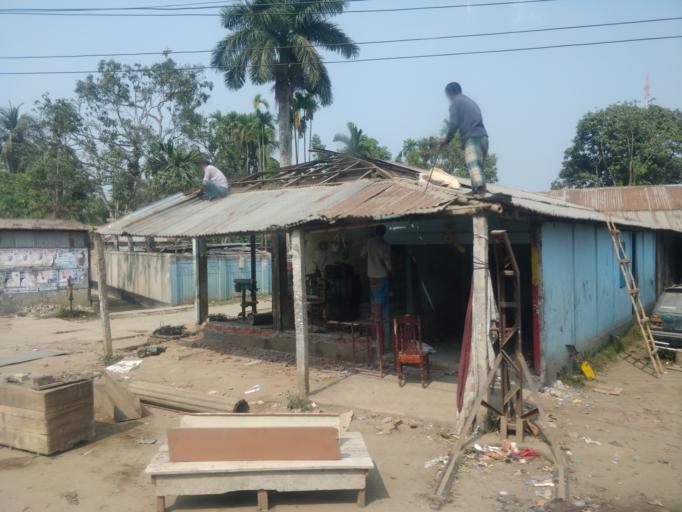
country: BD
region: Sylhet
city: Habiganj
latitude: 24.3647
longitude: 91.4179
